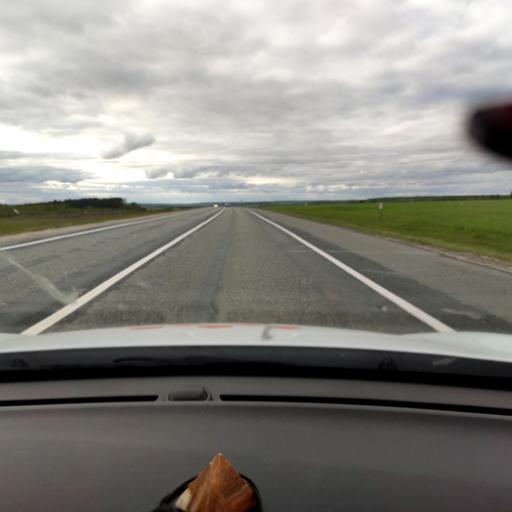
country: RU
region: Tatarstan
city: Laishevo
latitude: 55.4954
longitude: 49.8387
